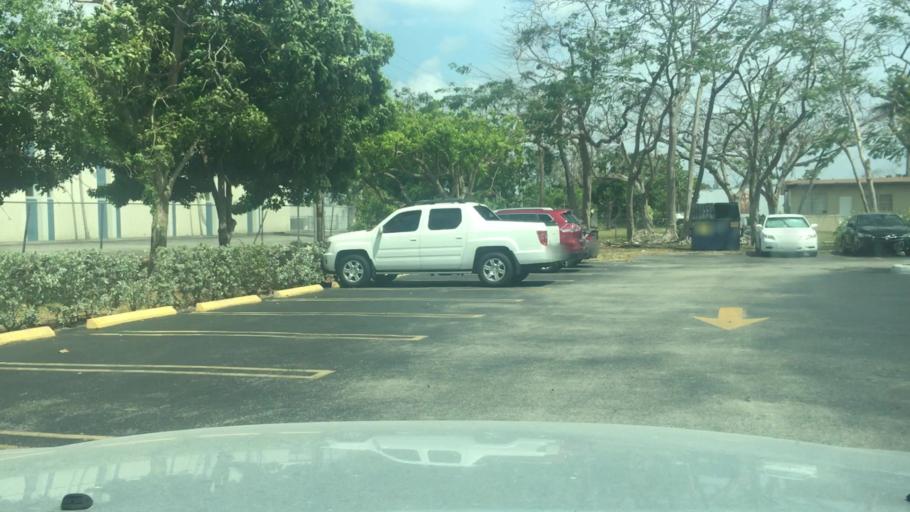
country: US
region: Florida
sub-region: Miami-Dade County
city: Westchester
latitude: 25.7556
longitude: -80.3378
